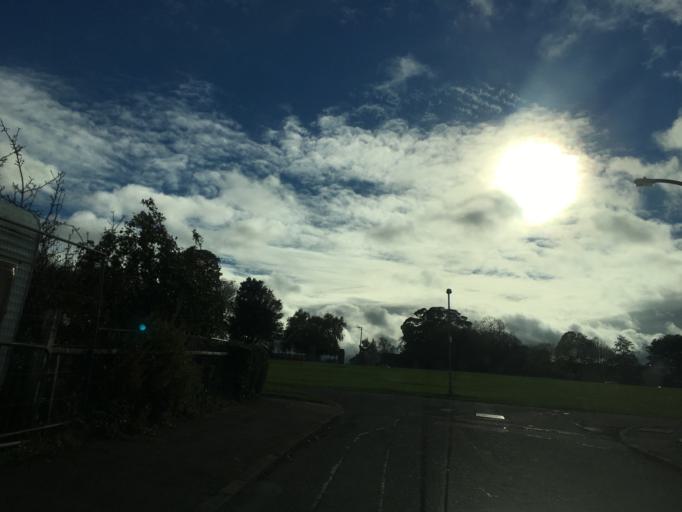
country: GB
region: Scotland
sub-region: Midlothian
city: Loanhead
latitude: 55.9162
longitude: -3.1584
